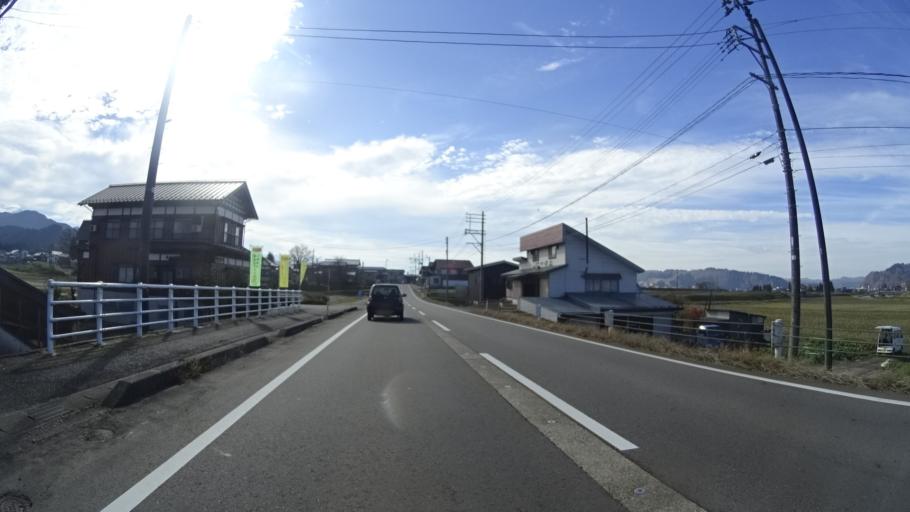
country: JP
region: Niigata
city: Ojiya
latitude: 37.2436
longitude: 138.9816
